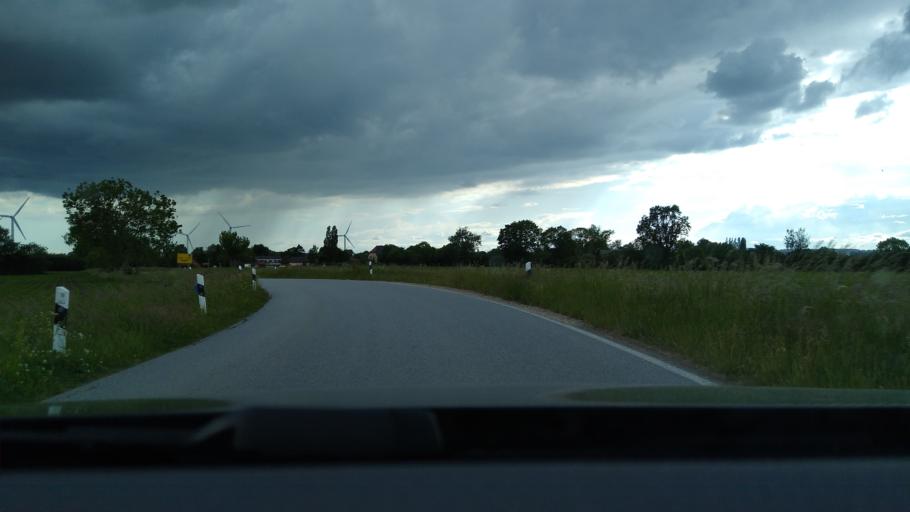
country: DE
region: Schleswig-Holstein
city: Riepsdorf
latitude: 54.2148
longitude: 10.9484
